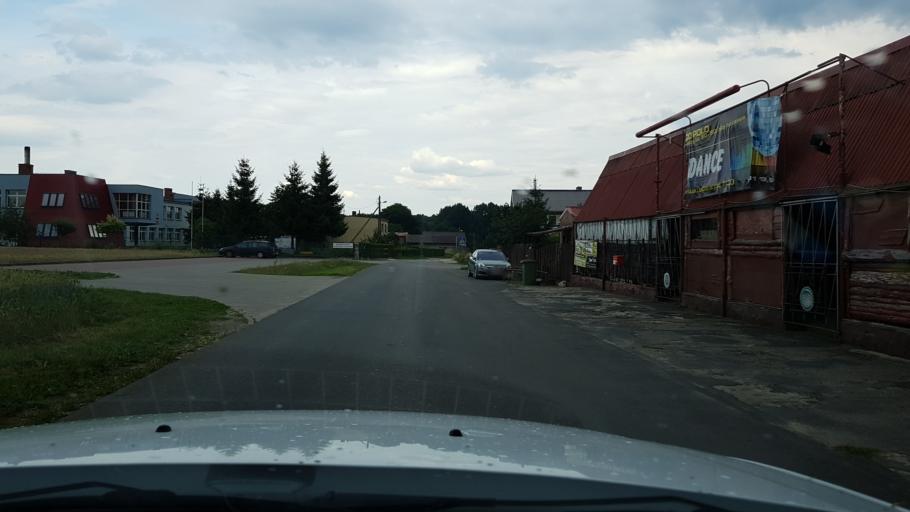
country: PL
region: West Pomeranian Voivodeship
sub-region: Powiat walecki
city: Walcz
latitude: 53.3516
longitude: 16.3935
